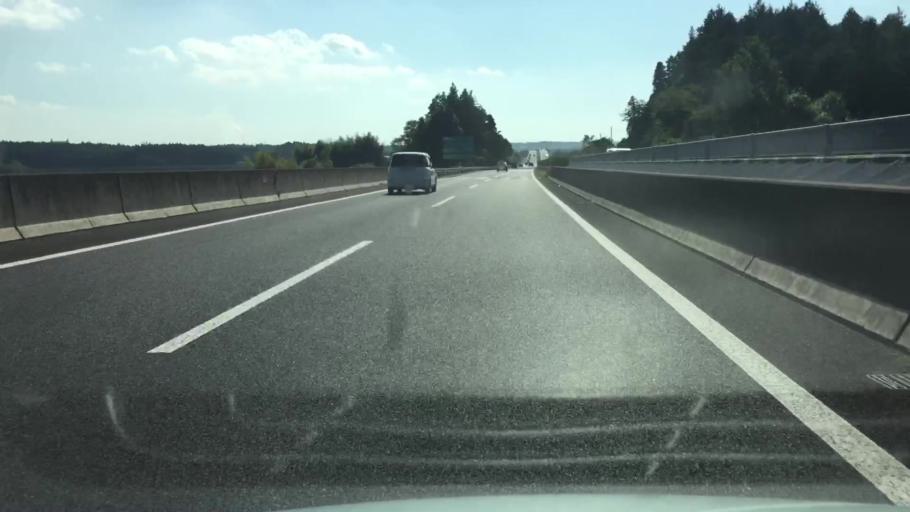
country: JP
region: Ibaraki
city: Tomobe
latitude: 36.3350
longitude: 140.2852
